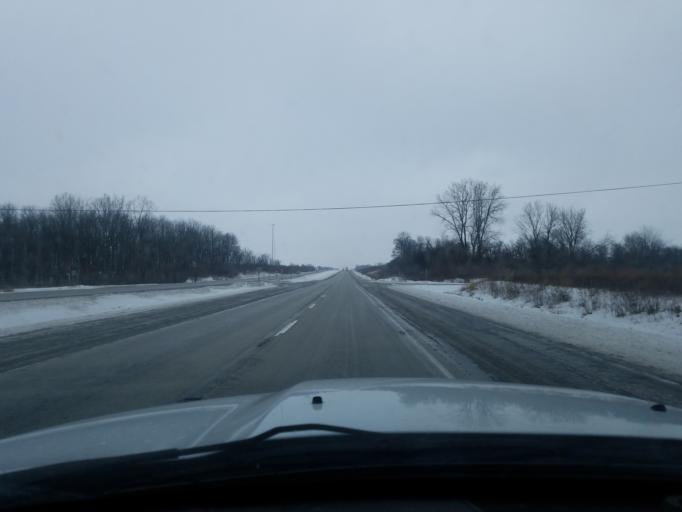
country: US
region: Indiana
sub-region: Fulton County
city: Rochester
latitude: 41.1340
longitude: -86.2397
